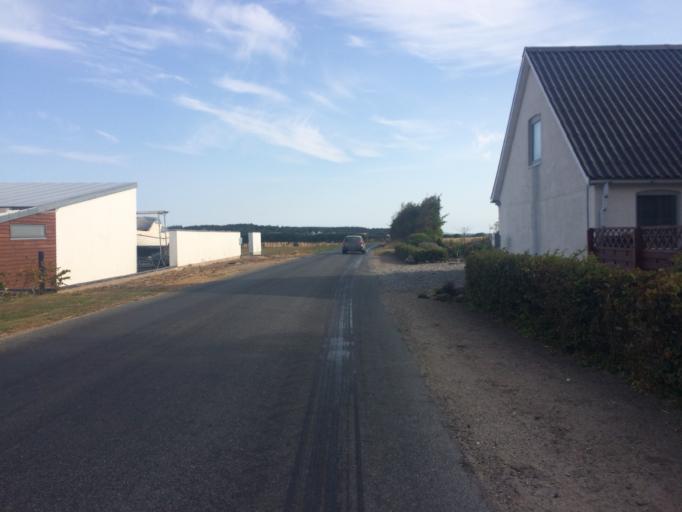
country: DK
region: Central Jutland
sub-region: Holstebro Kommune
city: Vinderup
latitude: 56.5927
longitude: 8.7566
